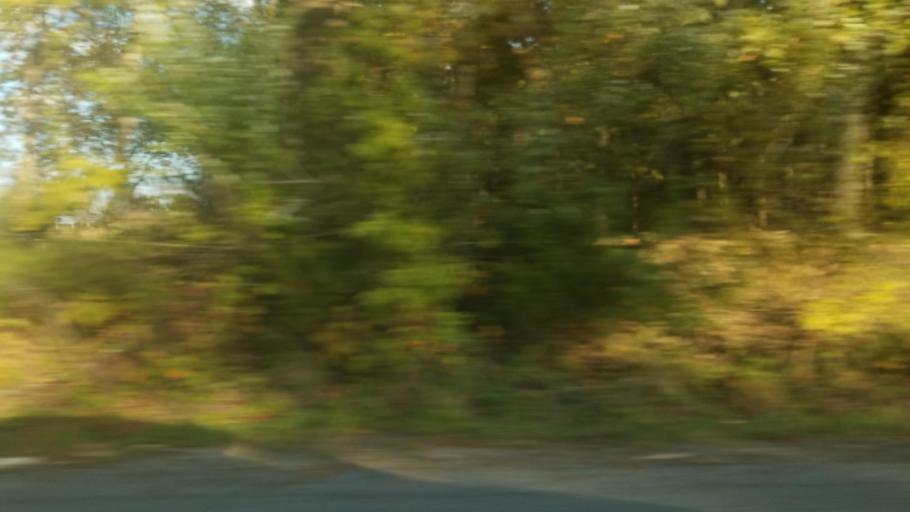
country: US
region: Illinois
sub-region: Saline County
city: Carrier Mills
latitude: 37.7978
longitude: -88.7117
